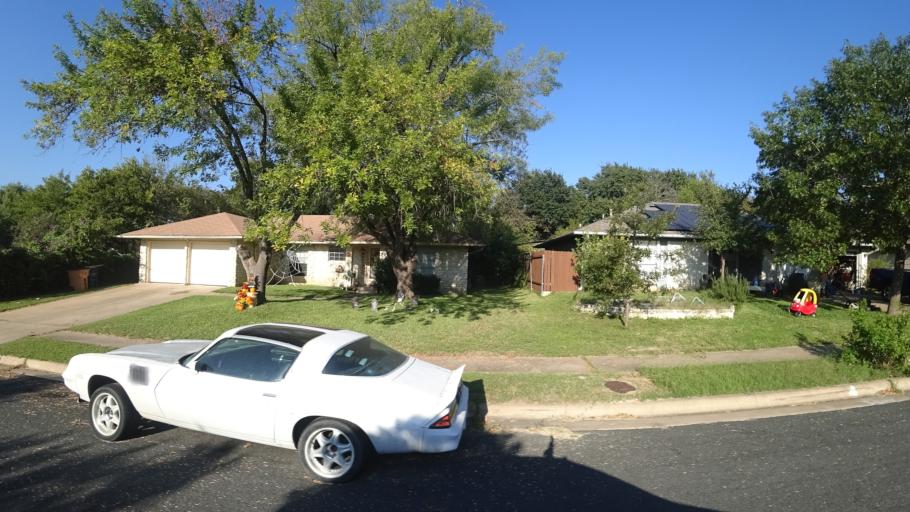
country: US
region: Texas
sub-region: Travis County
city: Wells Branch
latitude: 30.3572
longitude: -97.6741
